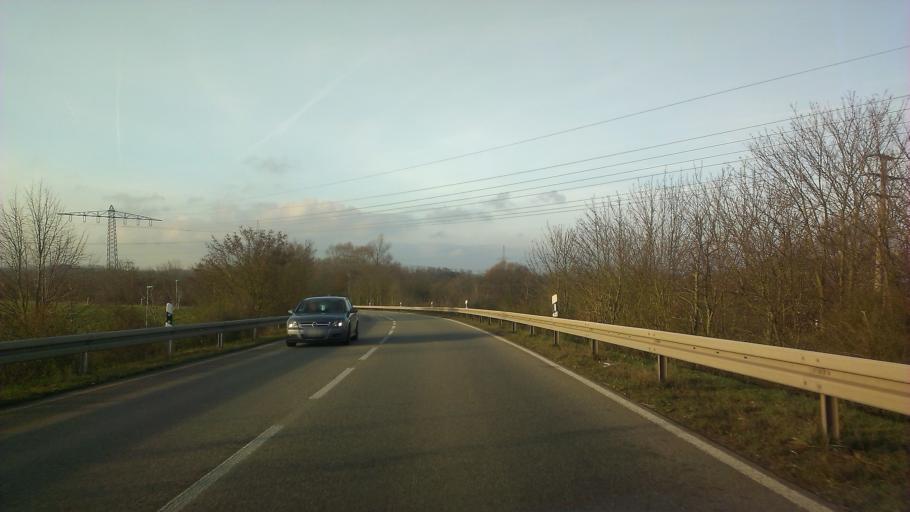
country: DE
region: Baden-Wuerttemberg
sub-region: Karlsruhe Region
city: Waghausel
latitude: 49.2543
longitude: 8.5142
